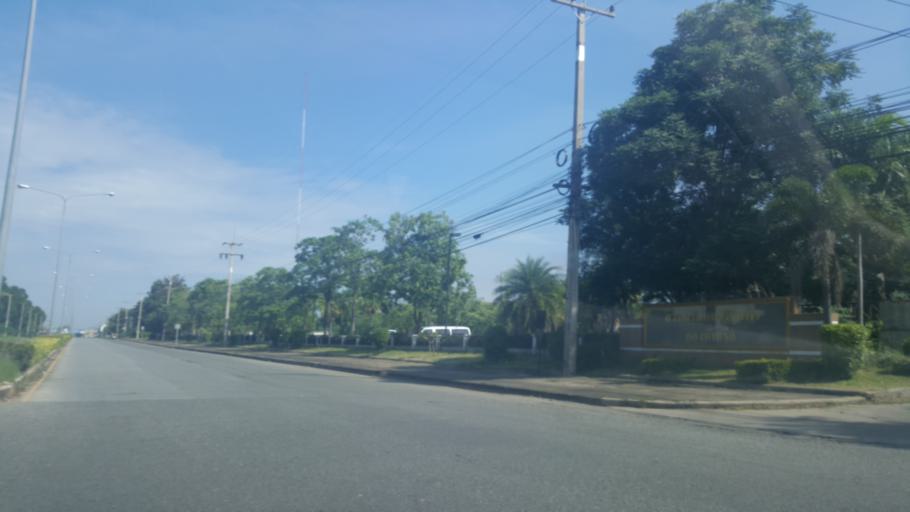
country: TH
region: Chon Buri
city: Sattahip
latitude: 12.6655
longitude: 100.8966
